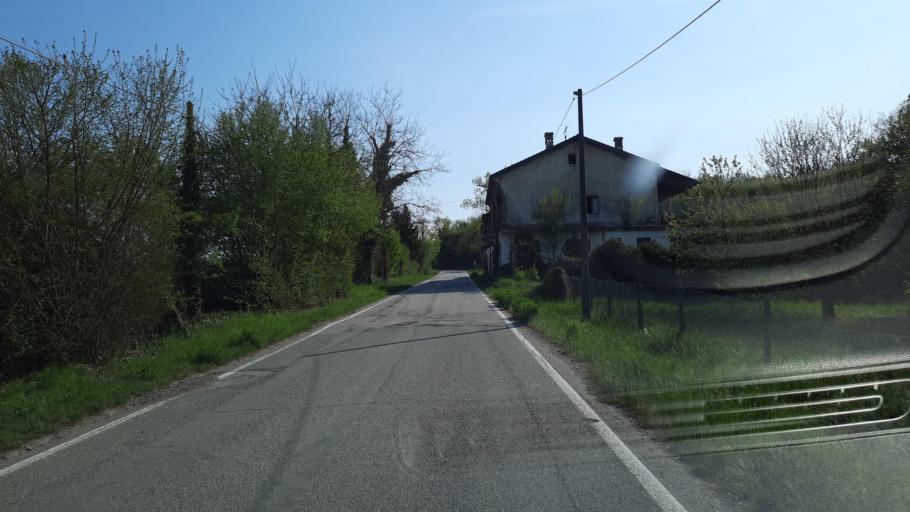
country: IT
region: Piedmont
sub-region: Provincia di Alessandria
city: Moncestino
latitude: 45.1577
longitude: 8.1770
